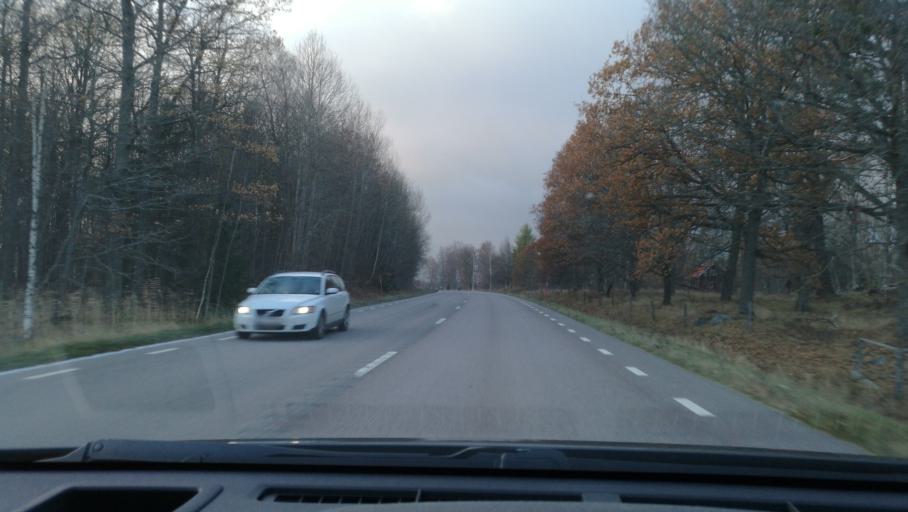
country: SE
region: Soedermanland
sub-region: Vingakers Kommun
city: Vingaker
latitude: 59.1576
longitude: 16.0252
